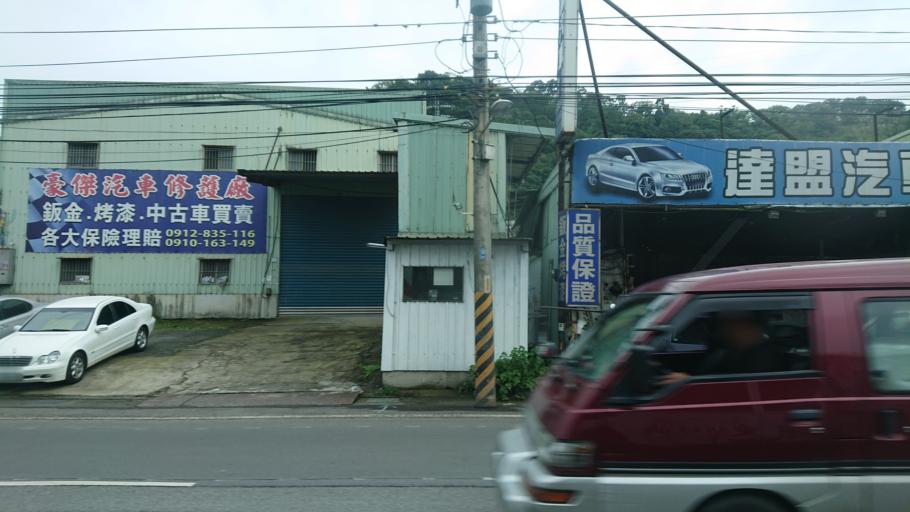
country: TW
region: Taiwan
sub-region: Taoyuan
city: Taoyuan
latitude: 24.9427
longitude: 121.4002
